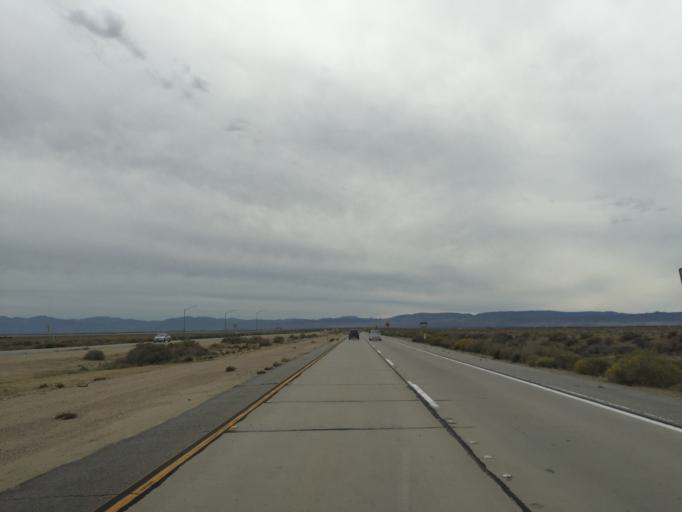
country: US
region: California
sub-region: Kern County
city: Rosamond
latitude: 34.8203
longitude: -118.1706
